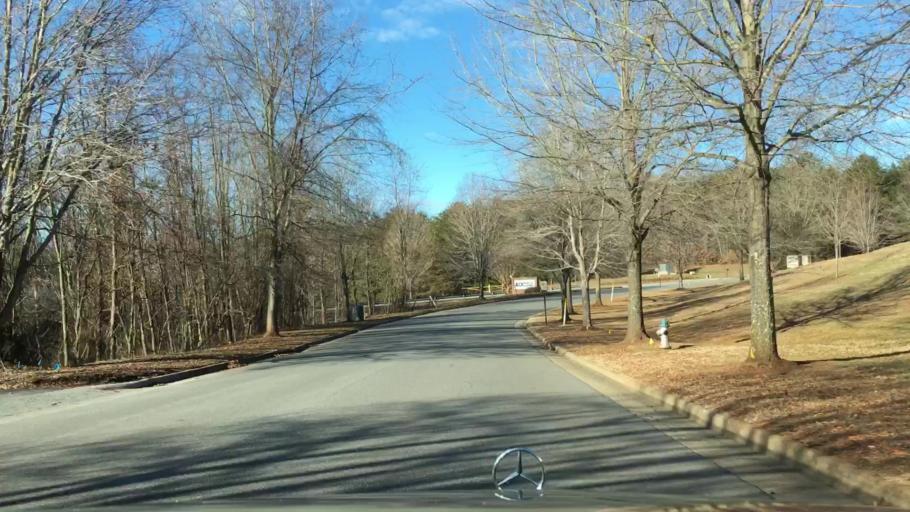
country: US
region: Virginia
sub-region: Bedford County
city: Forest
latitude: 37.3743
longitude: -79.2385
